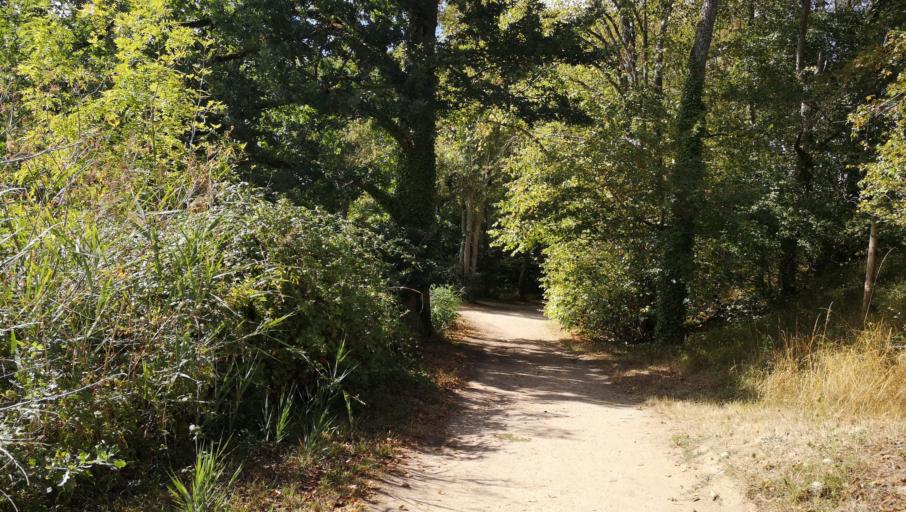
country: FR
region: Centre
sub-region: Departement du Loiret
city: Sully-sur-Loire
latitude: 47.7669
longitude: 2.3863
